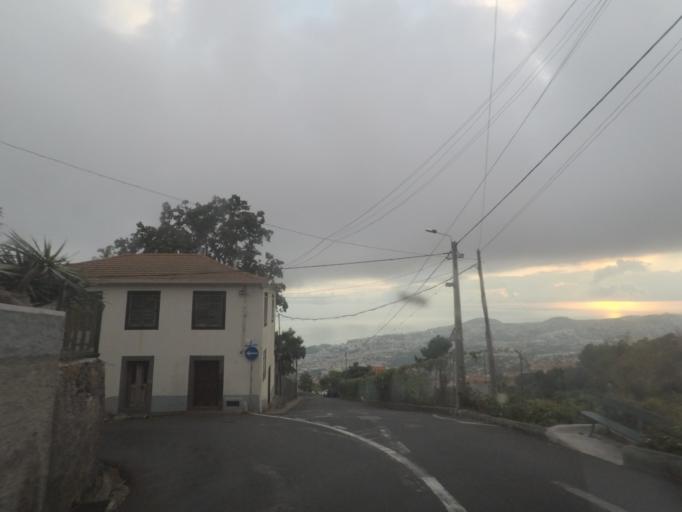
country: PT
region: Madeira
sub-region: Funchal
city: Nossa Senhora do Monte
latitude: 32.6719
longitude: -16.9048
